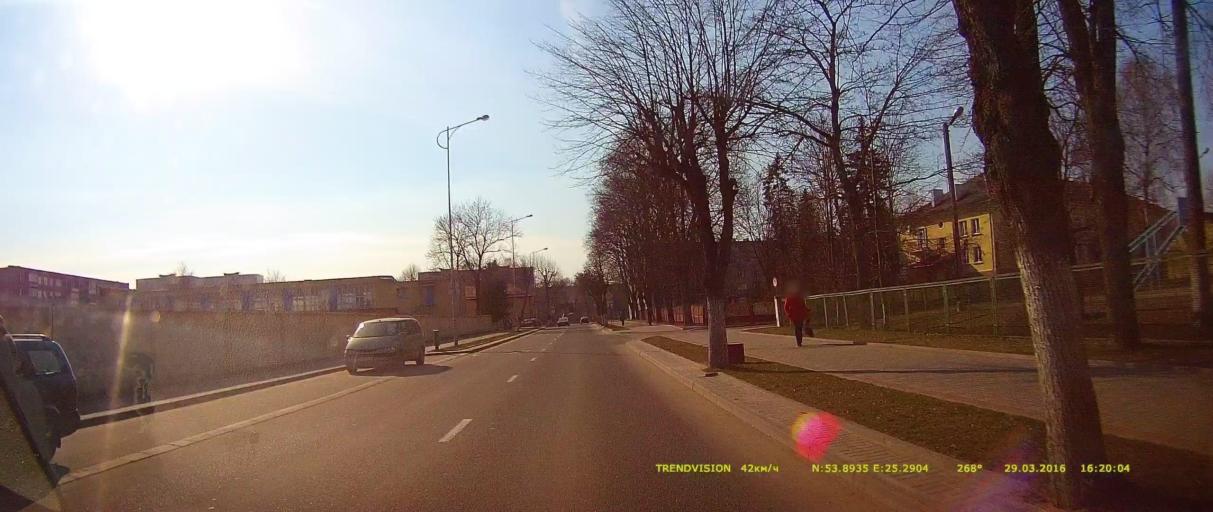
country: BY
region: Grodnenskaya
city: Lida
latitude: 53.8935
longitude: 25.2901
